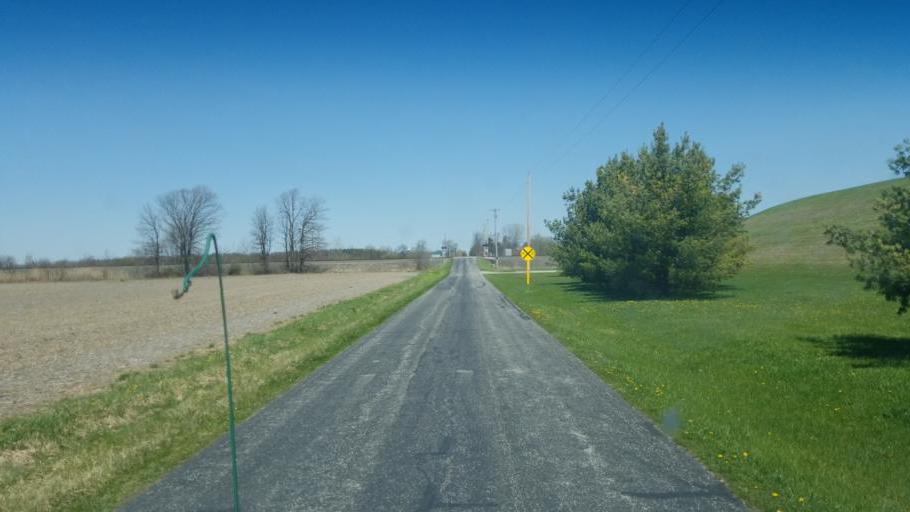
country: US
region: Ohio
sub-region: Huron County
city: New London
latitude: 41.0687
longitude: -82.4371
